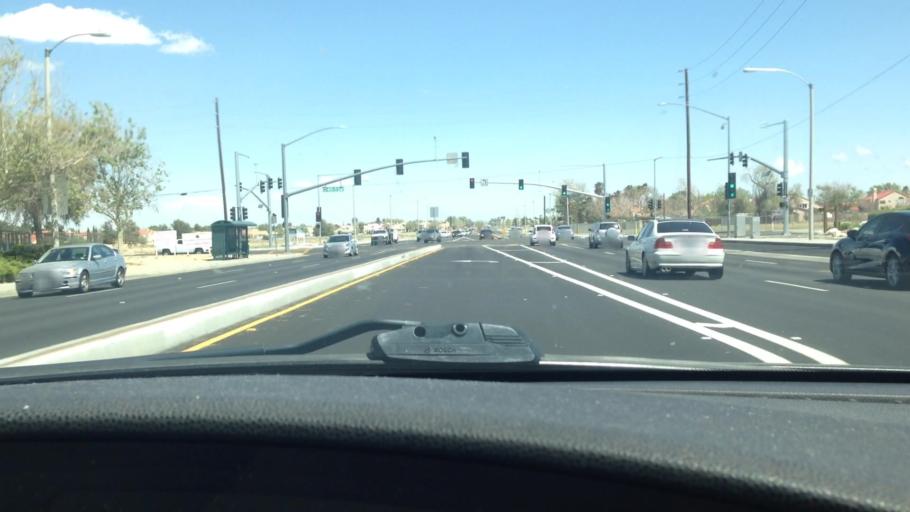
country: US
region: California
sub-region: Los Angeles County
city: Palmdale
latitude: 34.5581
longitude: -118.0596
